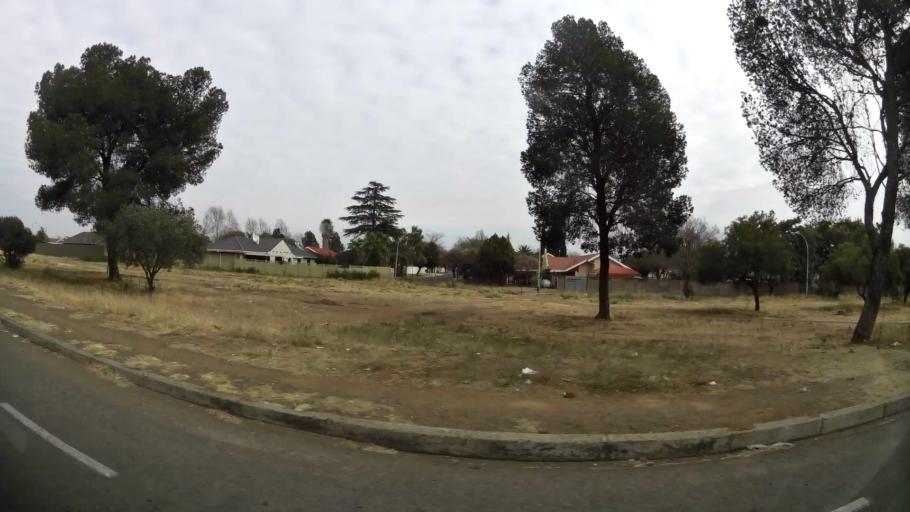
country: ZA
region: Orange Free State
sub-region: Mangaung Metropolitan Municipality
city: Bloemfontein
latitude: -29.1551
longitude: 26.1879
